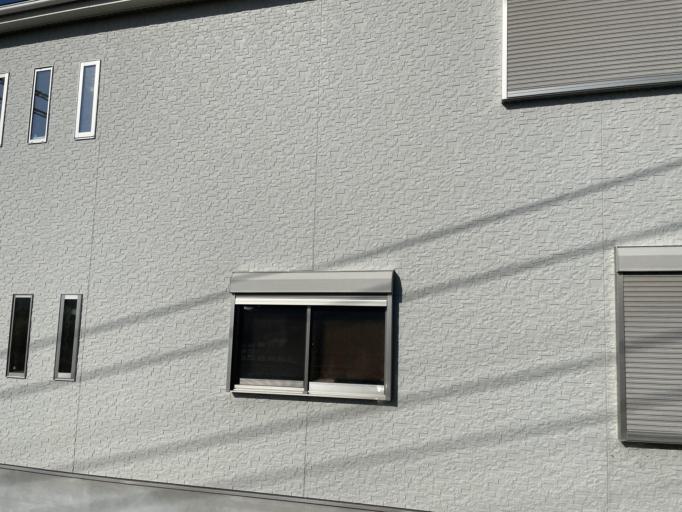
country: JP
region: Nara
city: Tawaramoto
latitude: 34.5475
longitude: 135.7926
